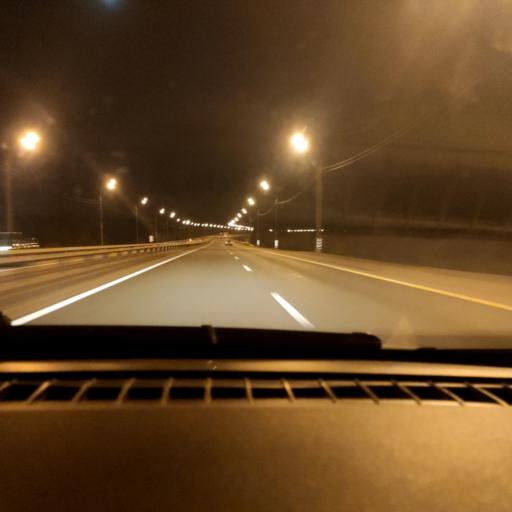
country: RU
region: Lipetsk
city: Khlevnoye
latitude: 52.1874
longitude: 39.1829
